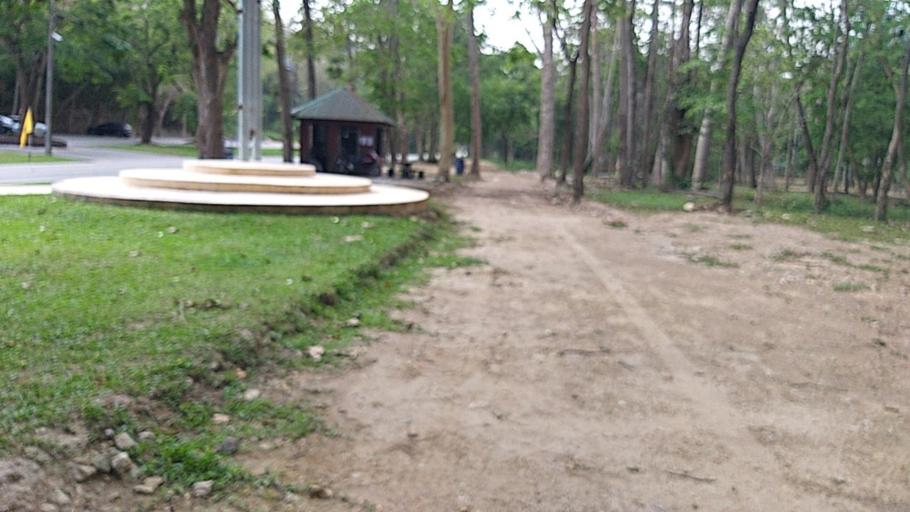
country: TH
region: Sara Buri
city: Wihan Daeng
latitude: 14.4379
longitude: 100.9622
